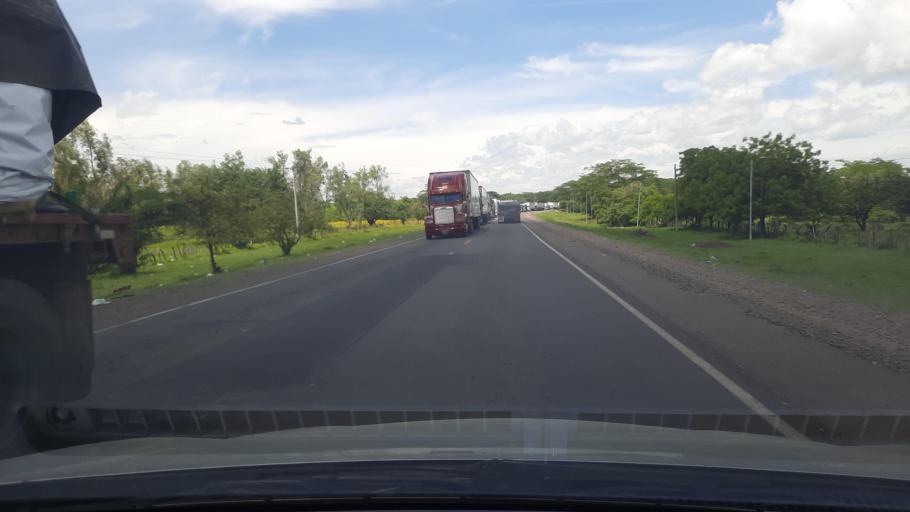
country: NI
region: Chinandega
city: Somotillo
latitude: 13.0592
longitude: -86.9336
